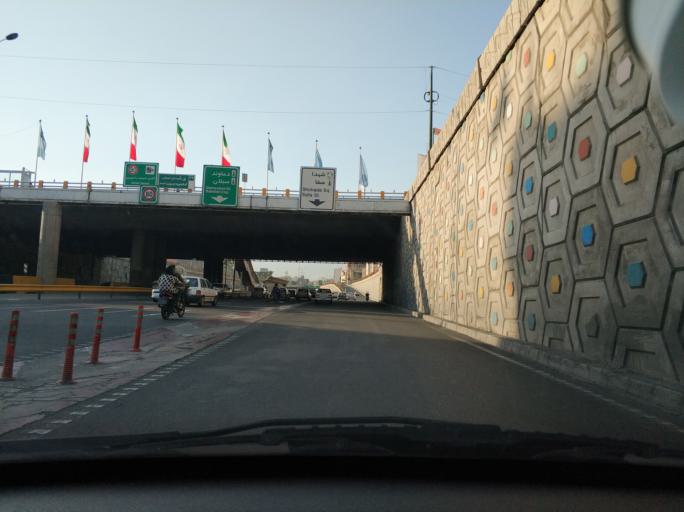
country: IR
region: Tehran
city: Tehran
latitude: 35.6898
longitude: 51.4574
